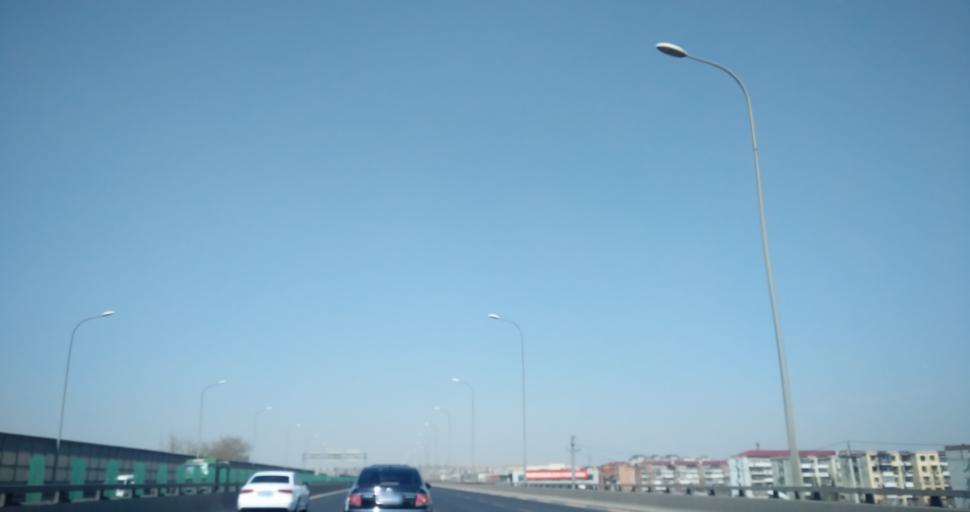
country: CN
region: Beijing
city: Jiugong
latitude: 39.7996
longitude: 116.4237
